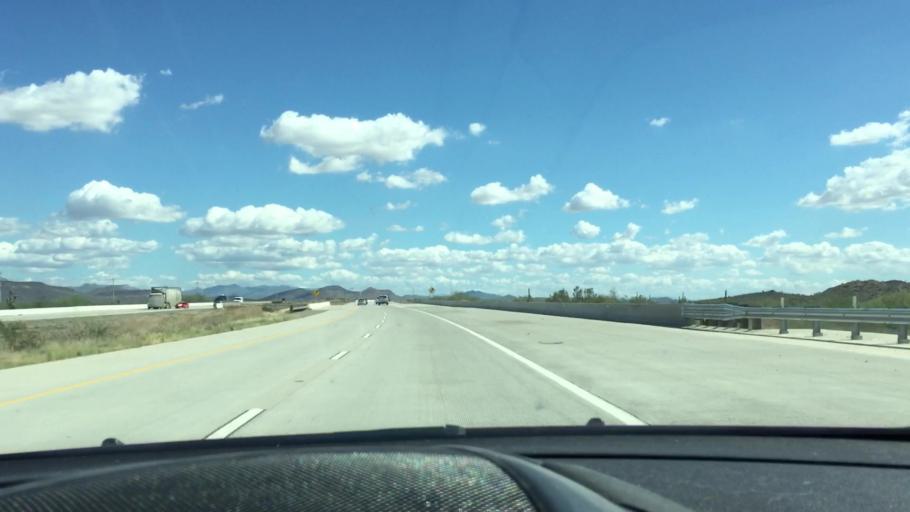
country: US
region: Arizona
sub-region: Maricopa County
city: Anthem
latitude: 33.7787
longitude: -112.2146
